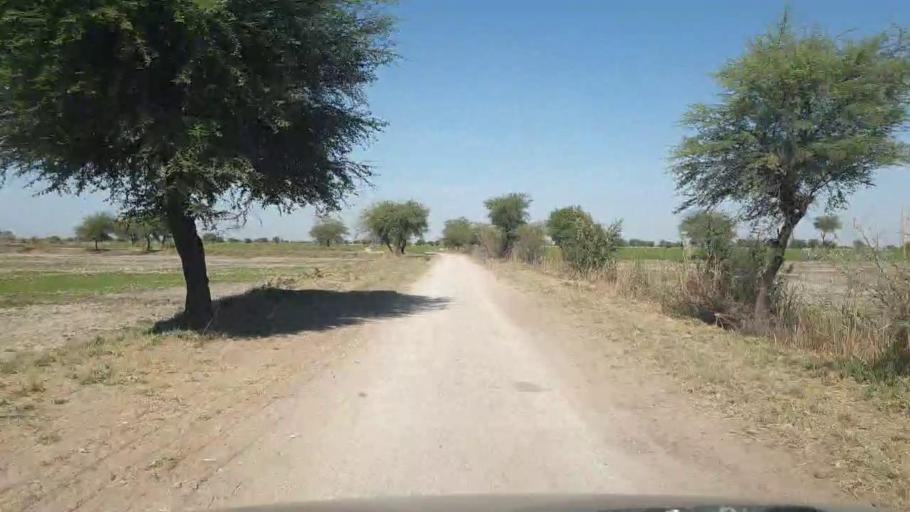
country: PK
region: Sindh
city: Dhoro Naro
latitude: 25.4482
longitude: 69.6154
